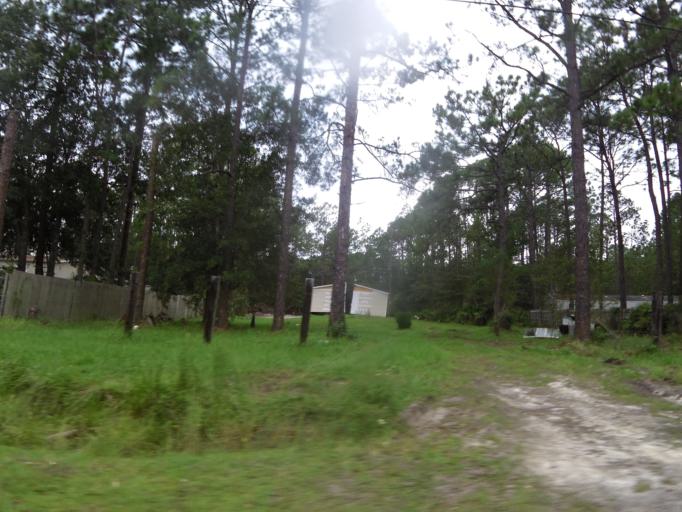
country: US
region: Florida
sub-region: Clay County
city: Middleburg
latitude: 30.0984
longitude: -81.9491
